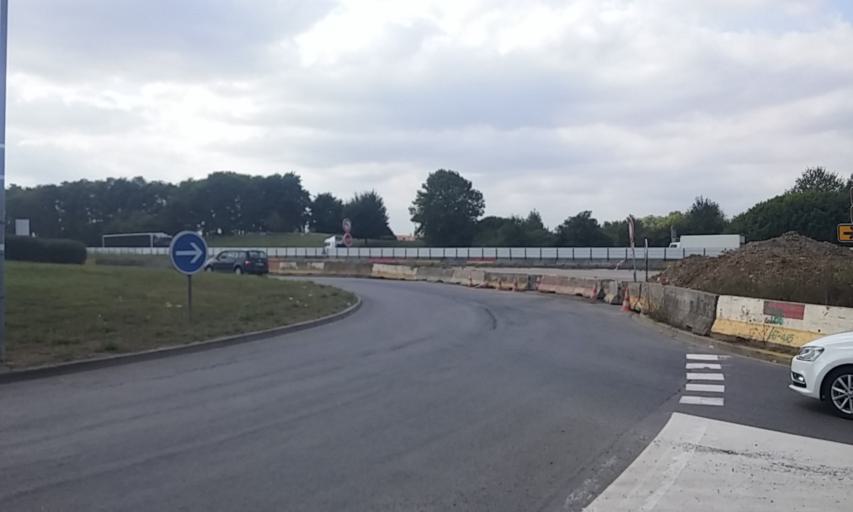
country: FR
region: Ile-de-France
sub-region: Departement de Seine-et-Marne
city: Emerainville
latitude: 48.8007
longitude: 2.6264
